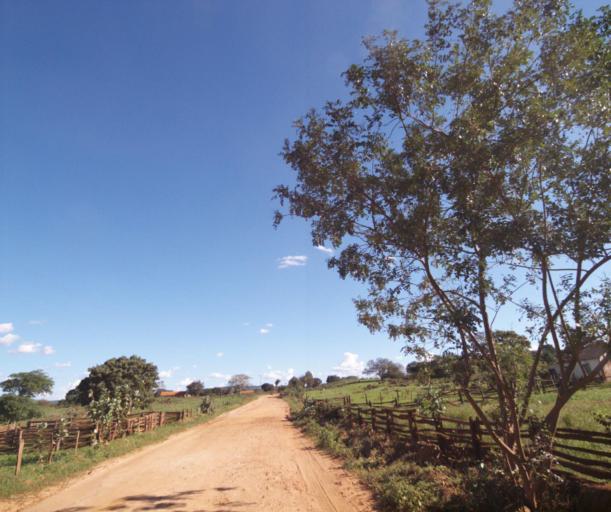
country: BR
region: Bahia
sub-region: Carinhanha
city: Carinhanha
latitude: -14.2491
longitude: -44.5245
